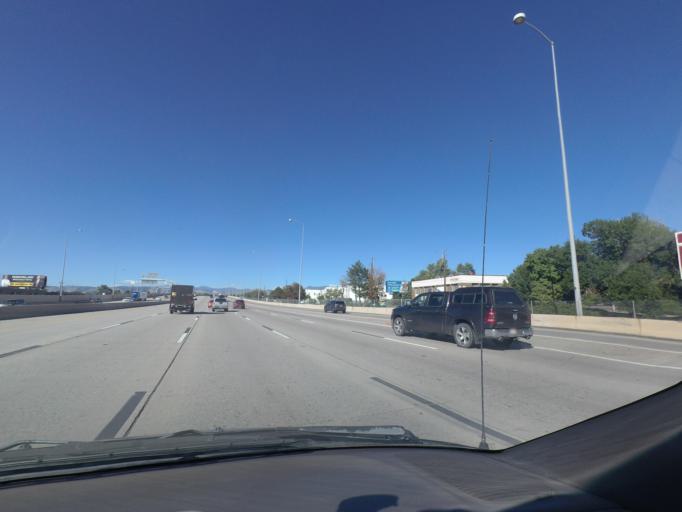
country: US
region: Colorado
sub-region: Jefferson County
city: Arvada
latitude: 39.7856
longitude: -105.0857
